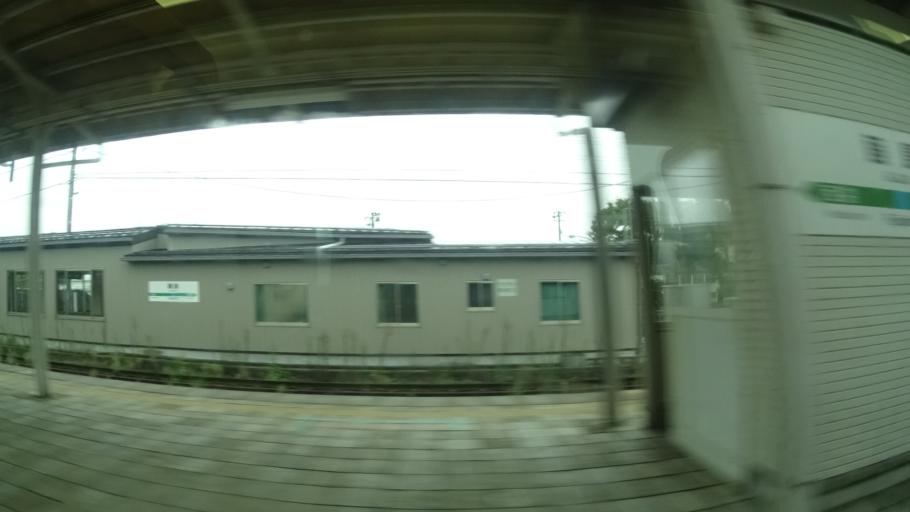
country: JP
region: Yamagata
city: Tsuruoka
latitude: 38.7689
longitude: 139.8944
